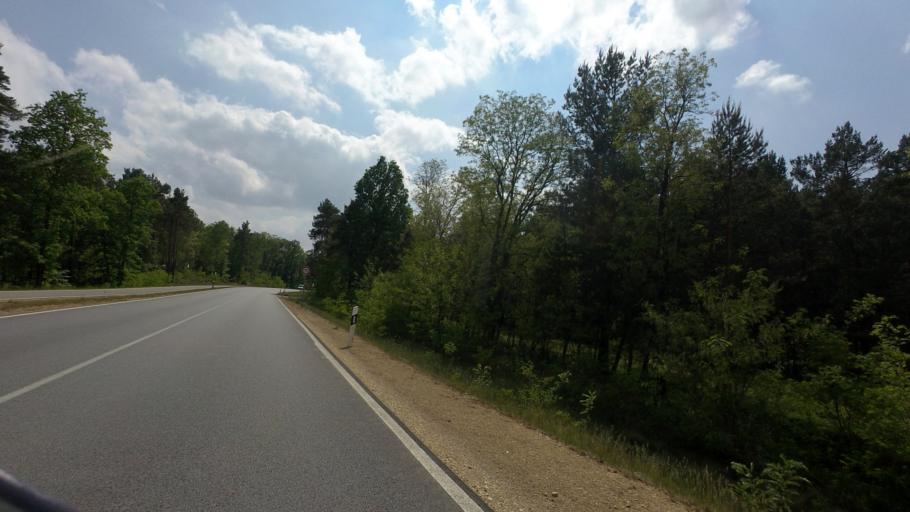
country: DE
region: Saxony
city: Rietschen
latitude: 51.4155
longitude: 14.7883
